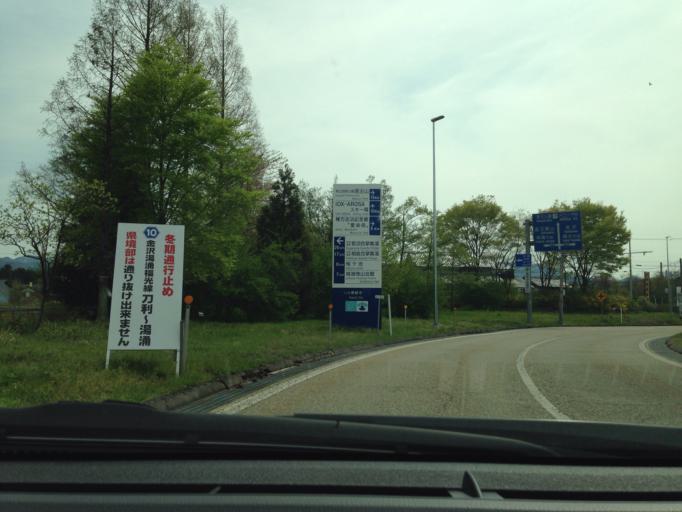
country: JP
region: Toyama
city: Fukumitsu
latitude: 36.5313
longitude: 136.8891
